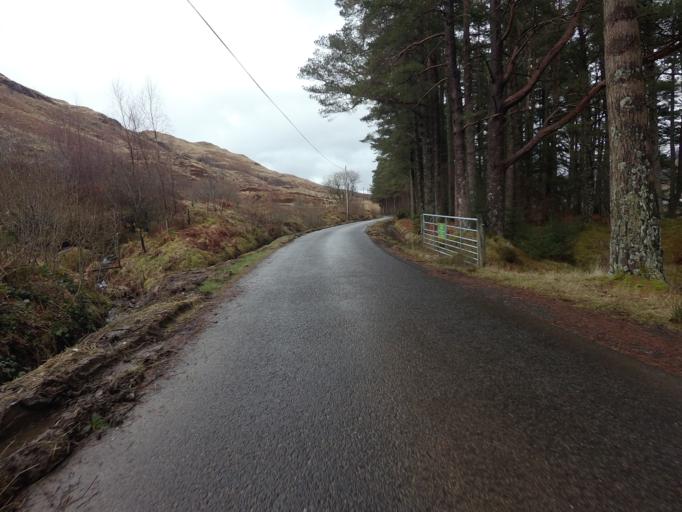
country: GB
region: Scotland
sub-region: Argyll and Bute
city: Garelochhead
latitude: 56.2499
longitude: -4.6521
